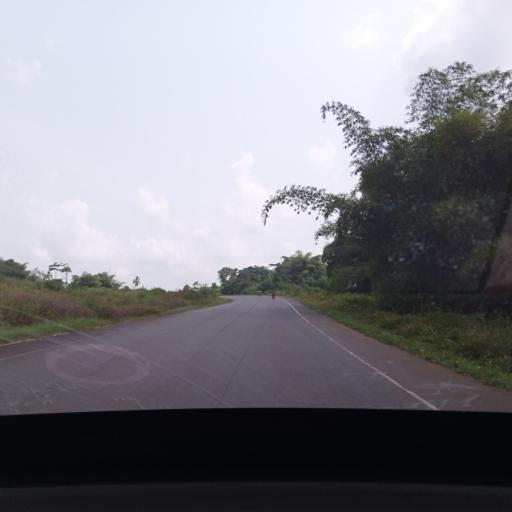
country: LR
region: Margibi
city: Kakata
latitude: 6.2531
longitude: -10.3060
